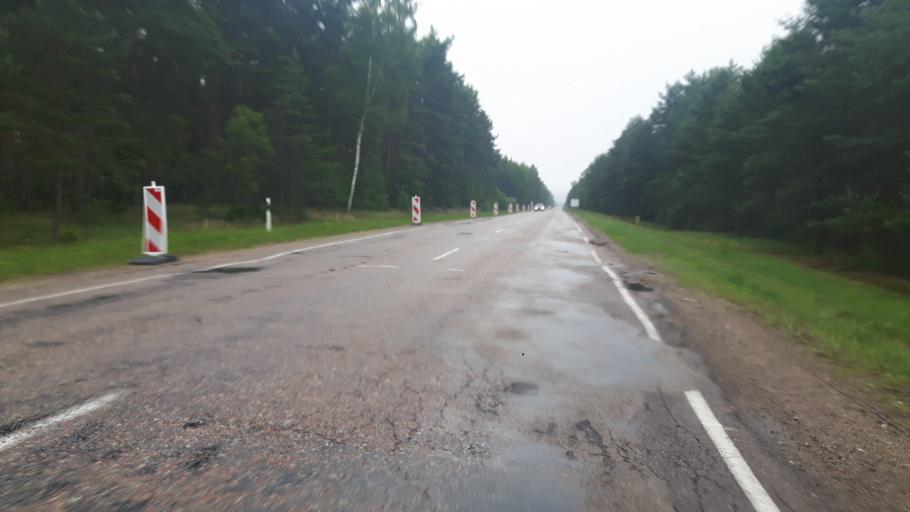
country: LV
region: Rucavas
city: Rucava
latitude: 56.1461
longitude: 21.1506
